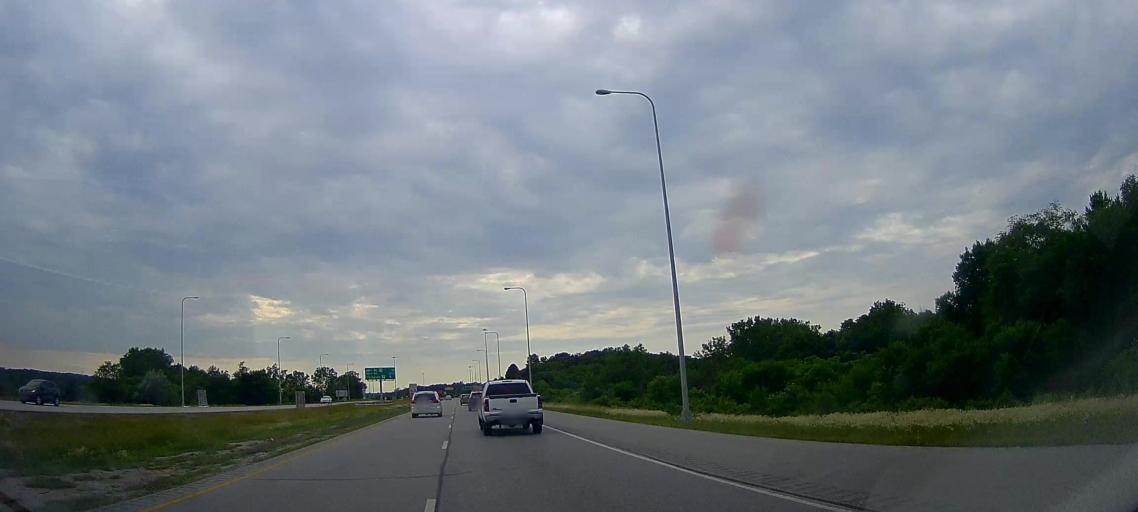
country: US
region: Iowa
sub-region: Pottawattamie County
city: Carter Lake
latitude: 41.3457
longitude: -95.9724
